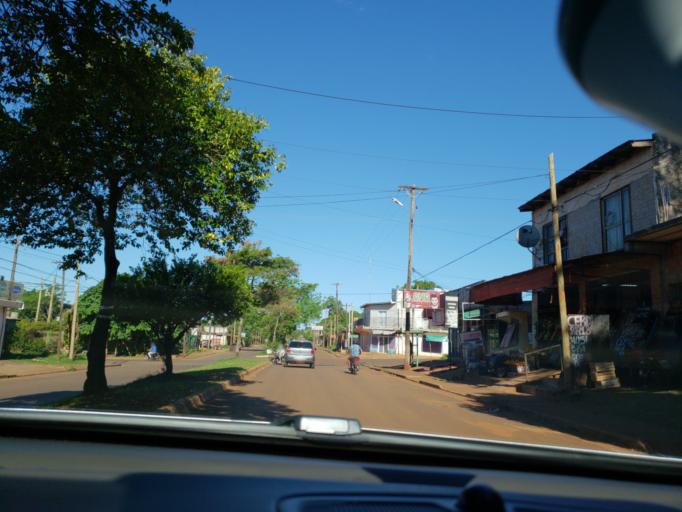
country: AR
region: Misiones
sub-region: Departamento de Capital
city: Posadas
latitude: -27.3843
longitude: -55.9309
